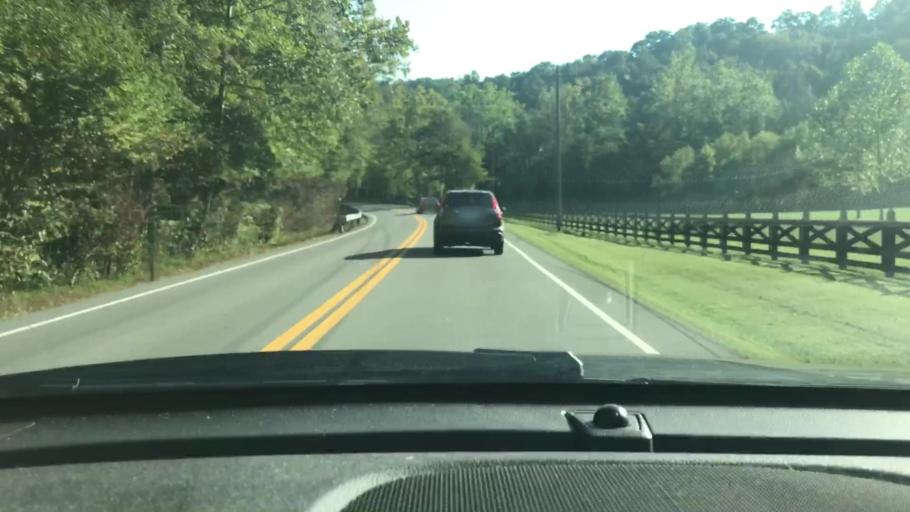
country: US
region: Tennessee
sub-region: Sumner County
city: White House
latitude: 36.4264
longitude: -86.6591
